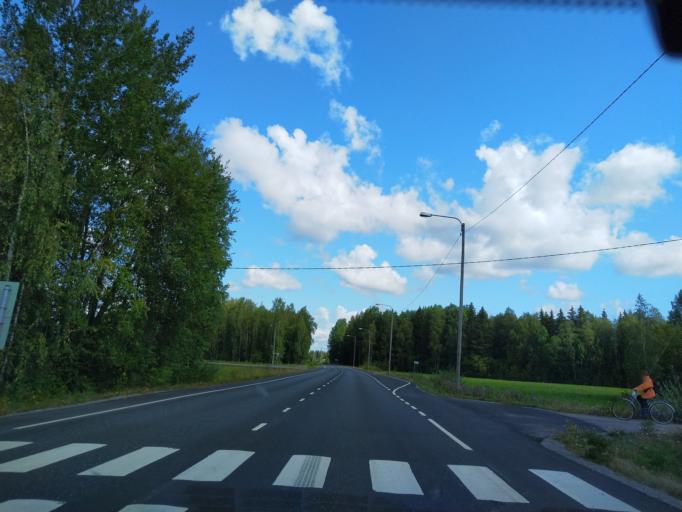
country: FI
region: Satakunta
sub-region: Pori
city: Huittinen
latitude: 61.1743
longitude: 22.7103
